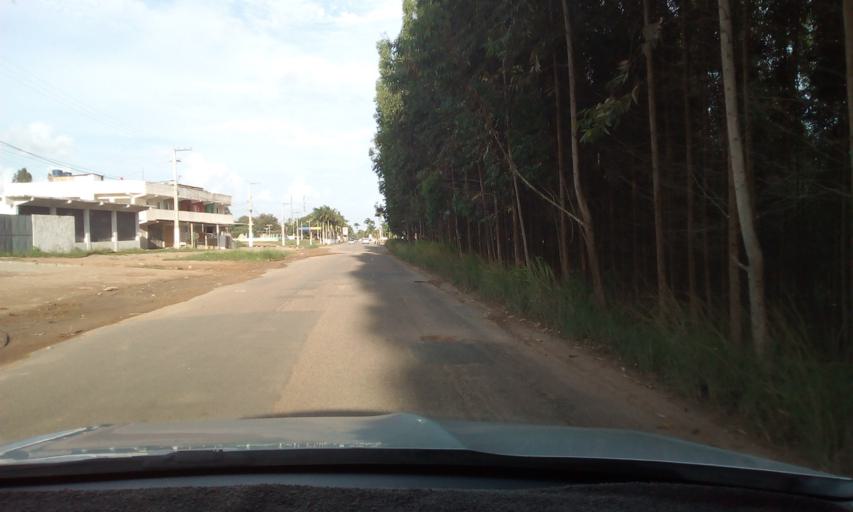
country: BR
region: Pernambuco
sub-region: Gloria Do Goita
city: Gloria do Goita
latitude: -7.9982
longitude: -35.2222
